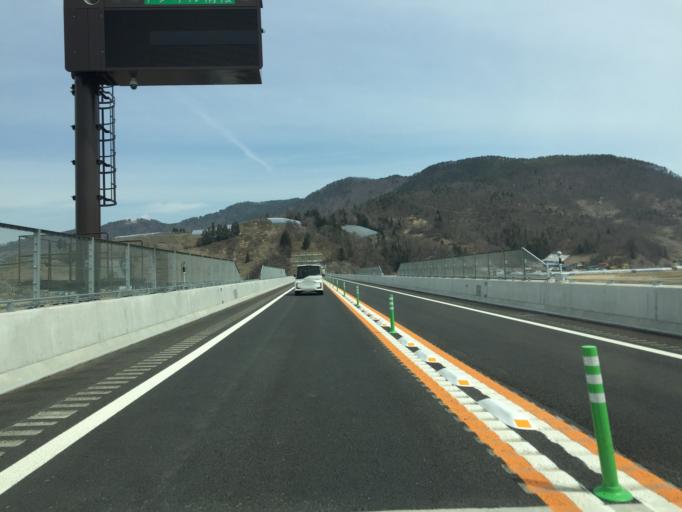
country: JP
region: Yamagata
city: Takahata
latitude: 38.0383
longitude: 140.1869
